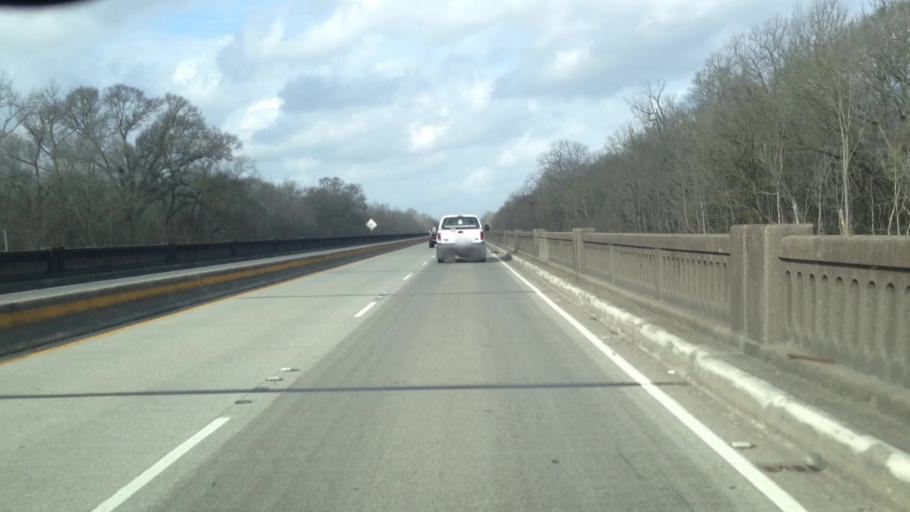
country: US
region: Louisiana
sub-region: Saint Landry Parish
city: Krotz Springs
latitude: 30.5556
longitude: -91.6760
